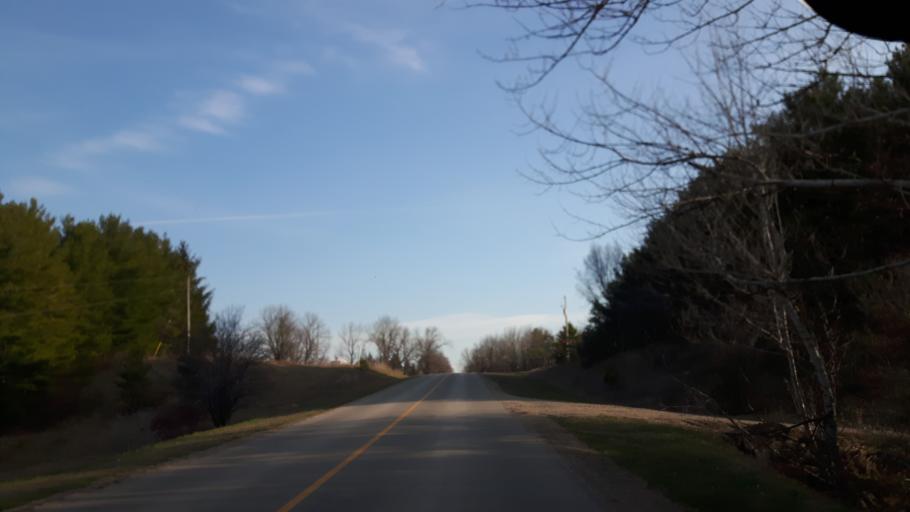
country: CA
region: Ontario
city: Goderich
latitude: 43.6710
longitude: -81.6644
